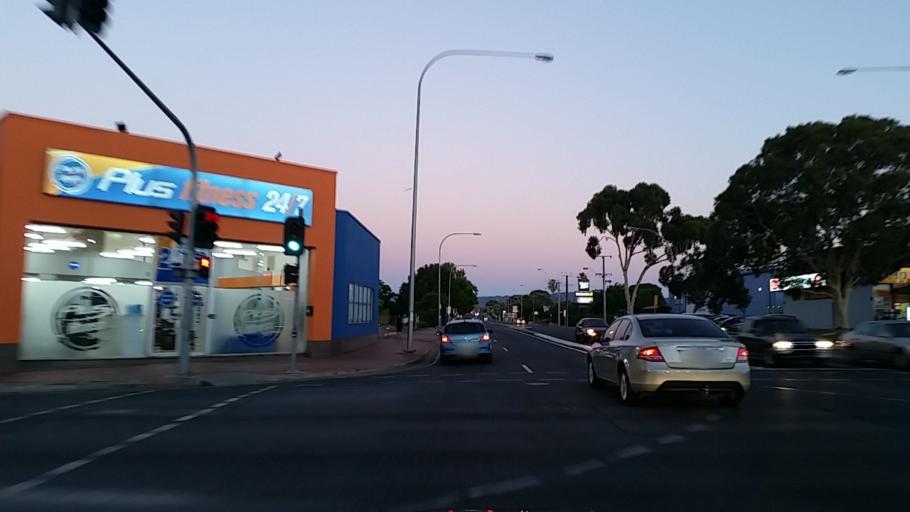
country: AU
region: South Australia
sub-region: Prospect
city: Prospect
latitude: -34.8736
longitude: 138.6019
